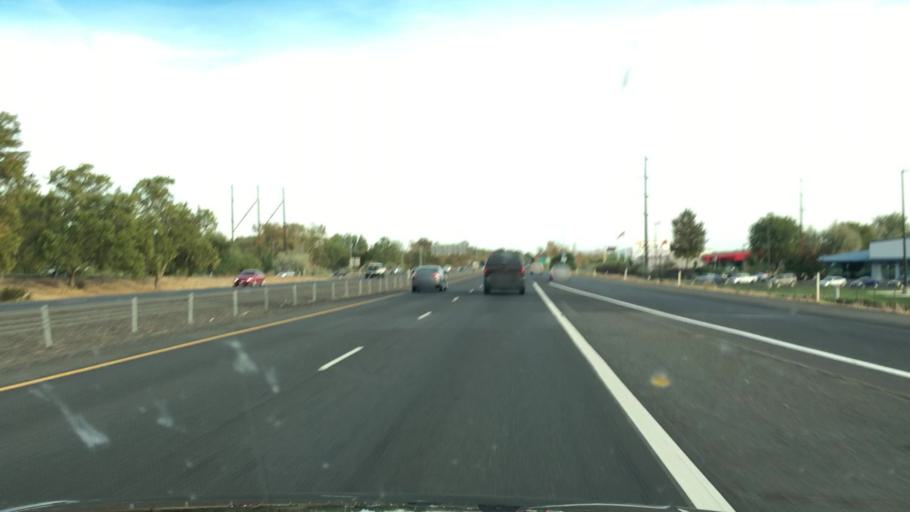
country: US
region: Washington
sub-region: Yakima County
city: Yakima
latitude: 46.6252
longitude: -120.5054
